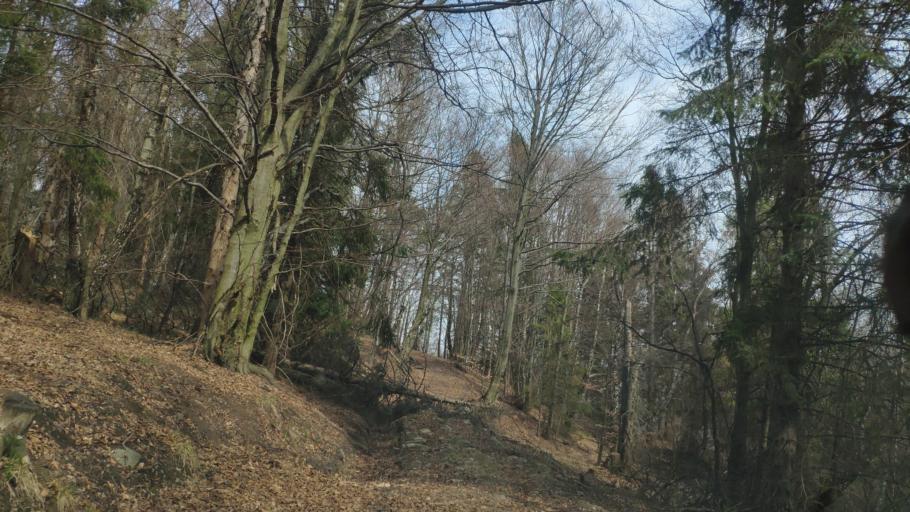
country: SK
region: Kosicky
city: Gelnica
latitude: 48.7602
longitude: 21.0198
